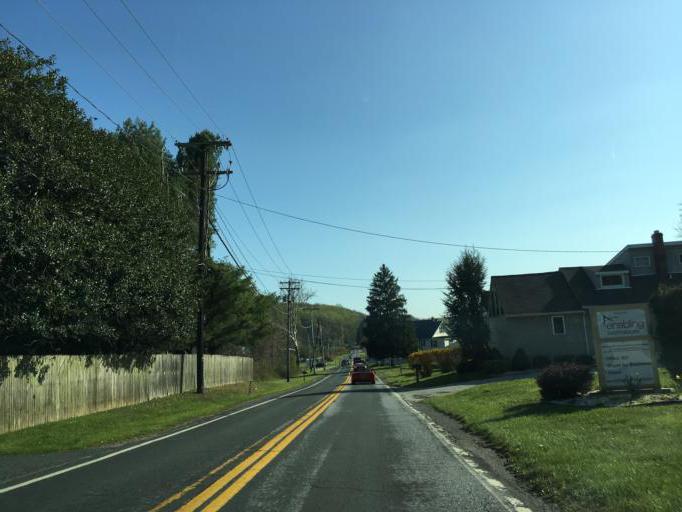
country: US
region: Maryland
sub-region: Baltimore County
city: Perry Hall
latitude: 39.4595
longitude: -76.4918
